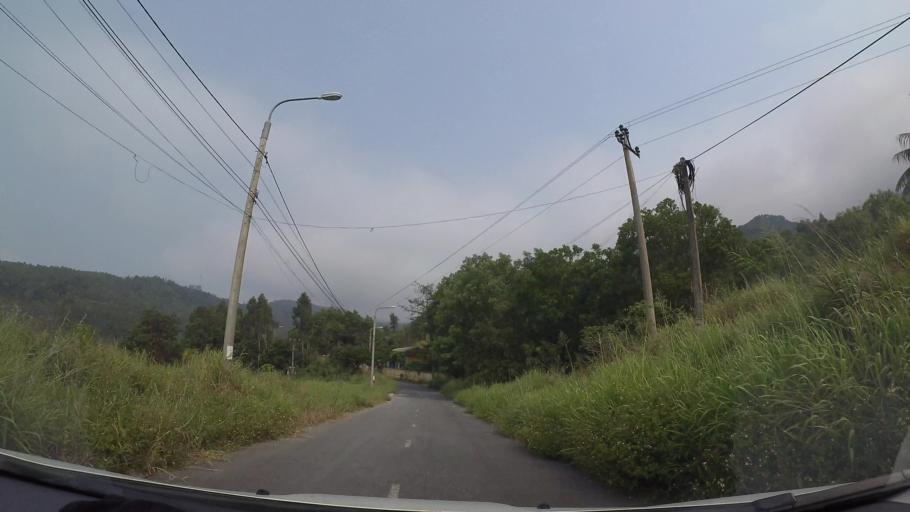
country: VN
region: Da Nang
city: Son Tra
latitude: 16.1086
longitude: 108.2613
